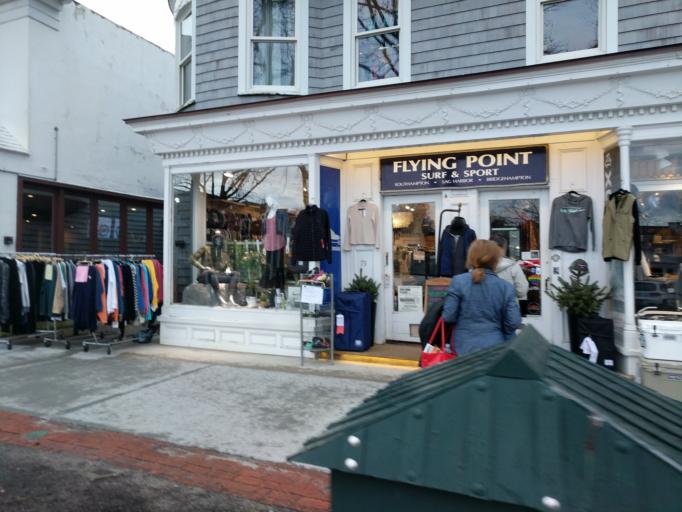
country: US
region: New York
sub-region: Suffolk County
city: Southampton
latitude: 40.8865
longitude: -72.3897
